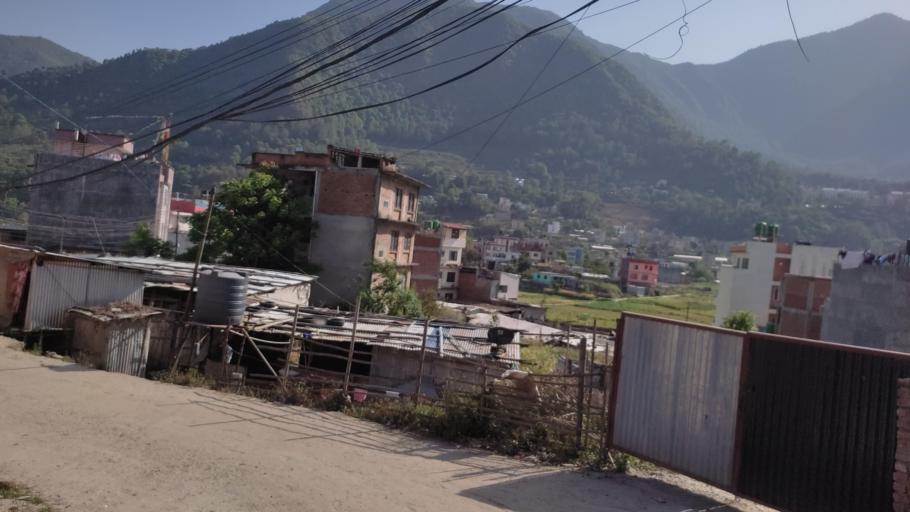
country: NP
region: Central Region
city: Kirtipur
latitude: 27.6646
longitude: 85.2654
